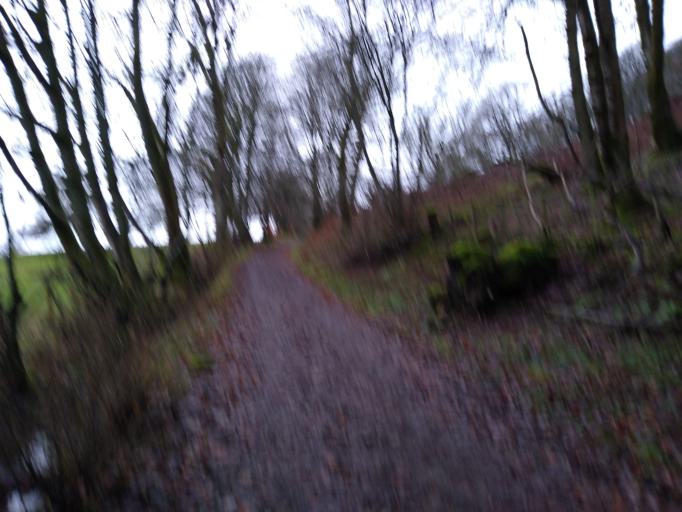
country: GB
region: England
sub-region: Cumbria
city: Penrith
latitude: 54.6132
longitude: -2.9209
